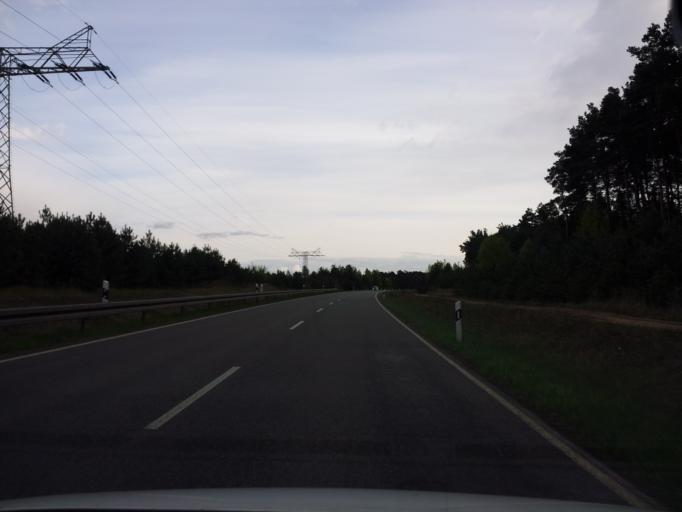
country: DE
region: Brandenburg
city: Heinersbruck
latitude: 51.8262
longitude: 14.5227
